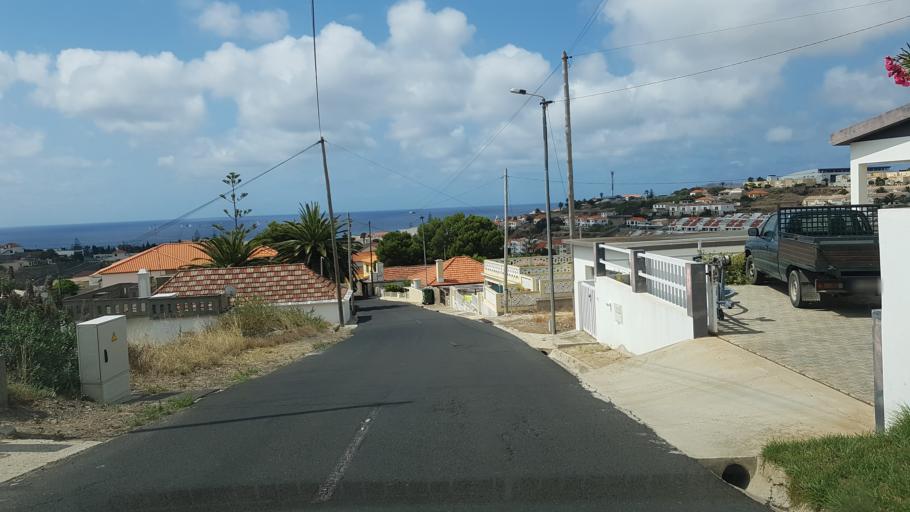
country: PT
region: Madeira
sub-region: Porto Santo
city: Vila de Porto Santo
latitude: 33.0665
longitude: -16.3334
